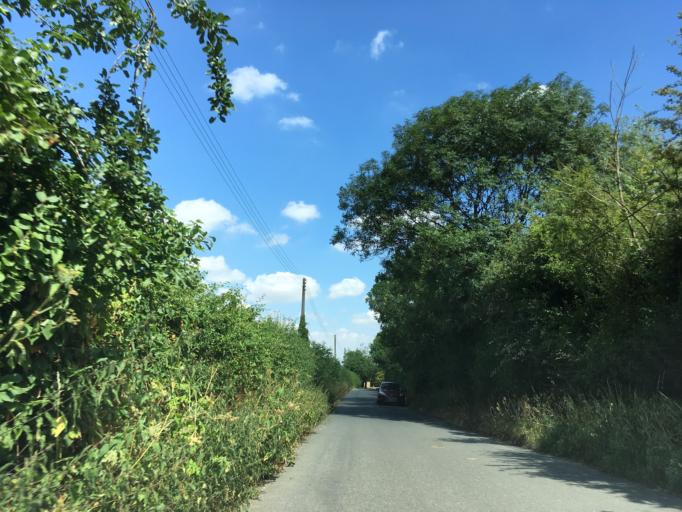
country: GB
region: England
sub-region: Gloucestershire
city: Shurdington
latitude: 51.8485
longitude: -2.1276
